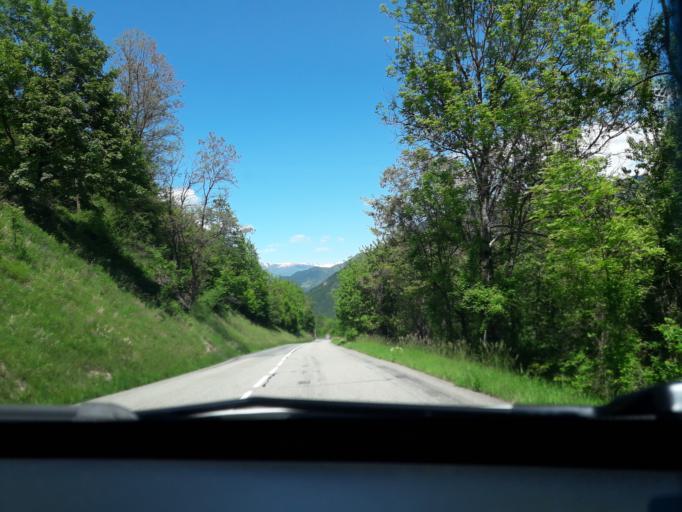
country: FR
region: Rhone-Alpes
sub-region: Departement de la Savoie
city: Salins-les-Thermes
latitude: 45.4530
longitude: 6.5064
